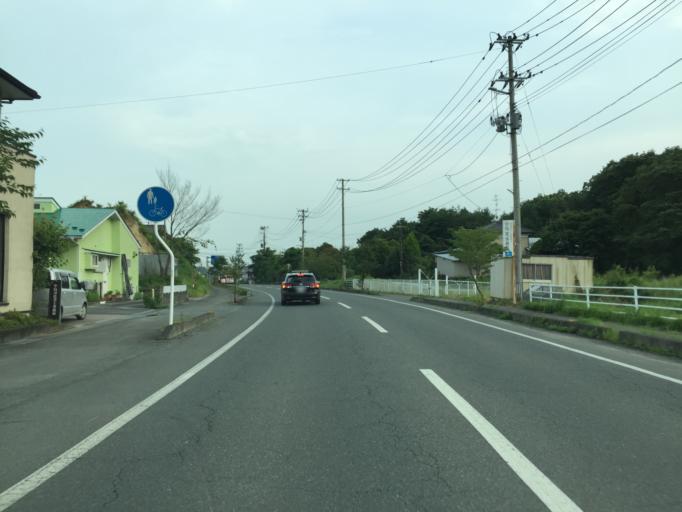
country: JP
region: Miyagi
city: Marumori
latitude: 37.7943
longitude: 140.9105
